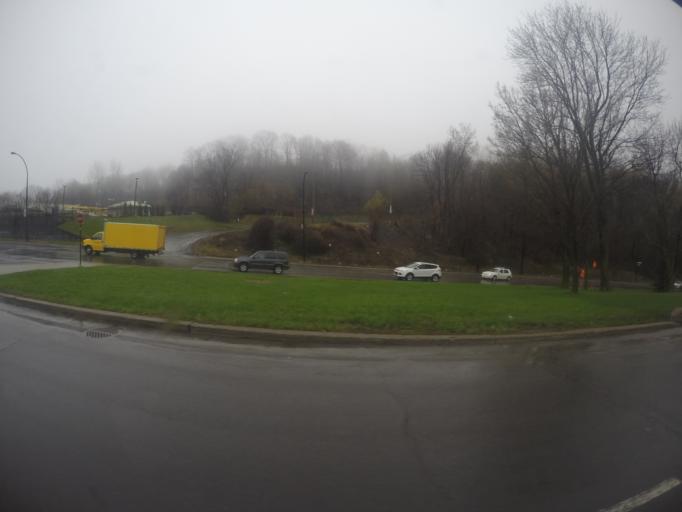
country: CA
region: Quebec
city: Saint-Raymond
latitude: 45.4715
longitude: -73.5995
